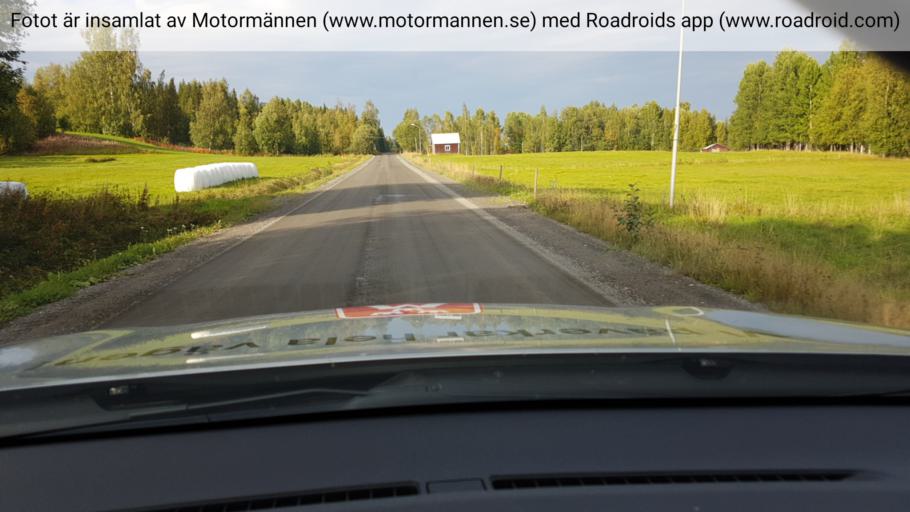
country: SE
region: Jaemtland
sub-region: Stroemsunds Kommun
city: Stroemsund
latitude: 64.0367
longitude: 15.8097
